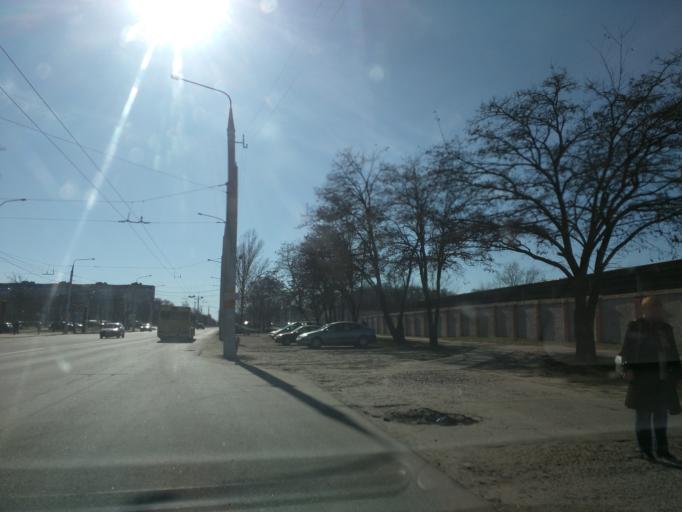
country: BY
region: Mogilev
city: Babruysk
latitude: 53.1792
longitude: 29.2009
